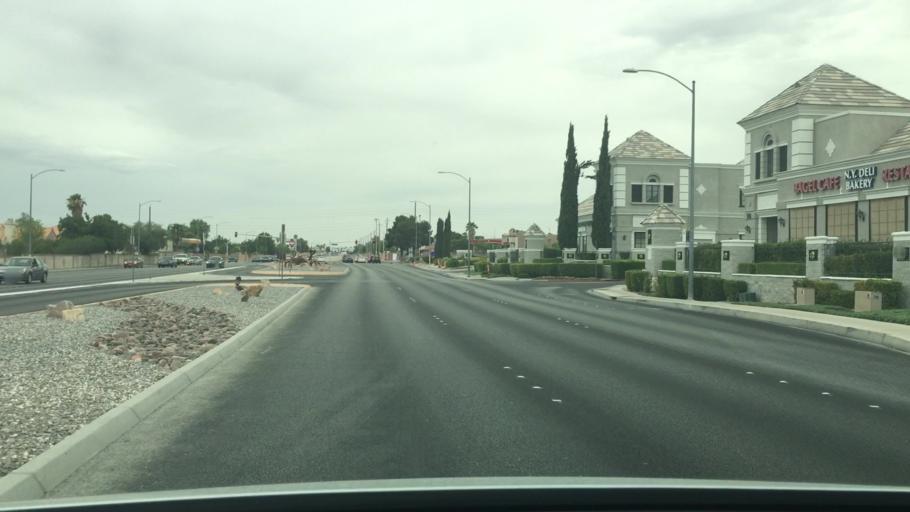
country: US
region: Nevada
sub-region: Clark County
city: Spring Valley
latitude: 36.1764
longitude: -115.2599
